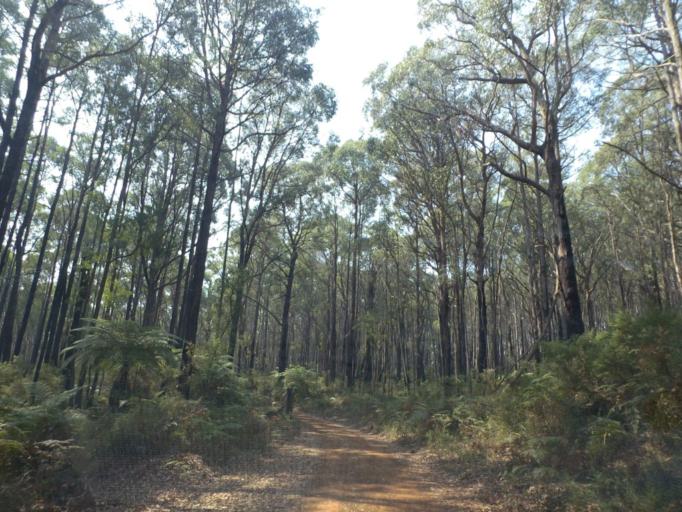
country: AU
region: Victoria
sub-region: Yarra Ranges
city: Millgrove
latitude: -37.5797
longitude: 145.6866
